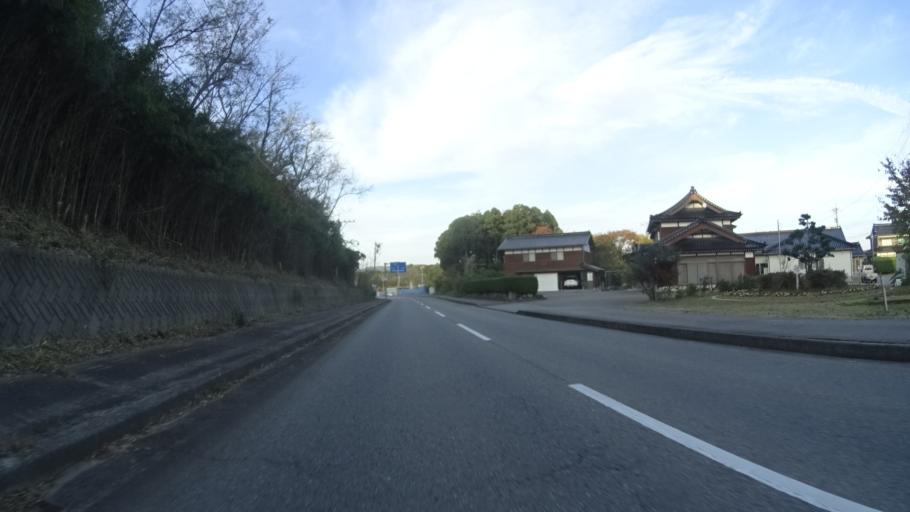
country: JP
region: Ishikawa
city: Nanao
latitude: 37.1523
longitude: 136.7203
